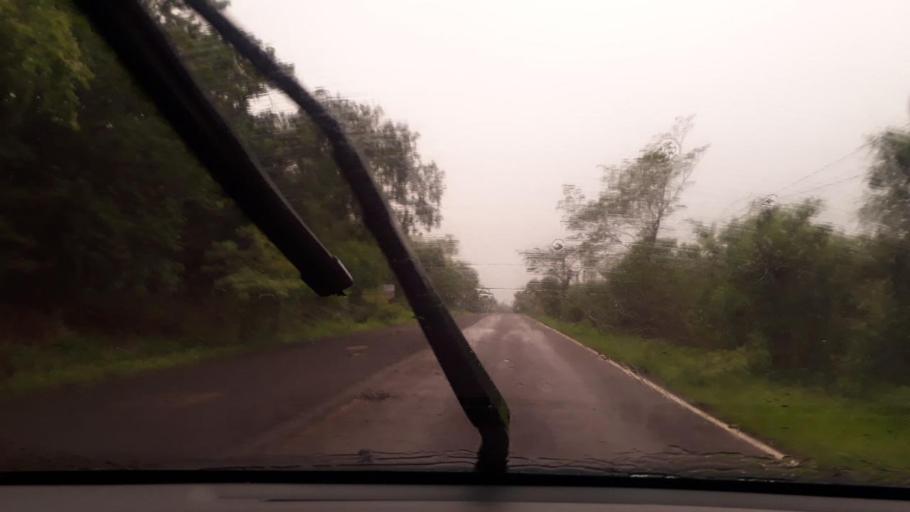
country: GT
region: Jutiapa
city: Comapa
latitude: 14.0786
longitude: -89.9562
